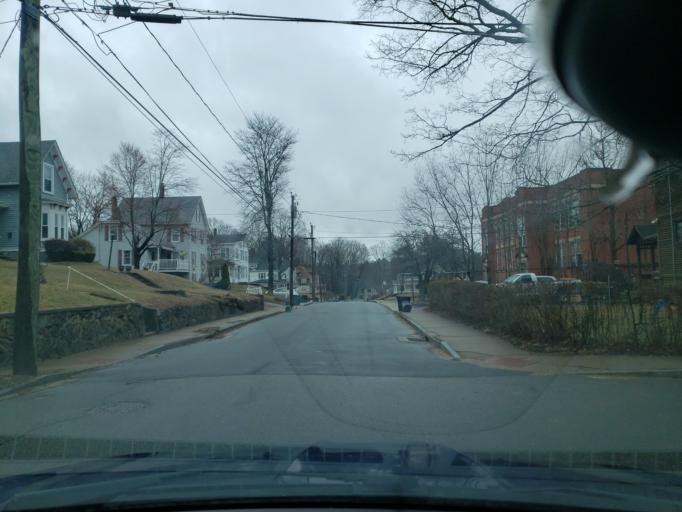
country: US
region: Connecticut
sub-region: Tolland County
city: Stafford Springs
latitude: 41.9561
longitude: -72.3070
